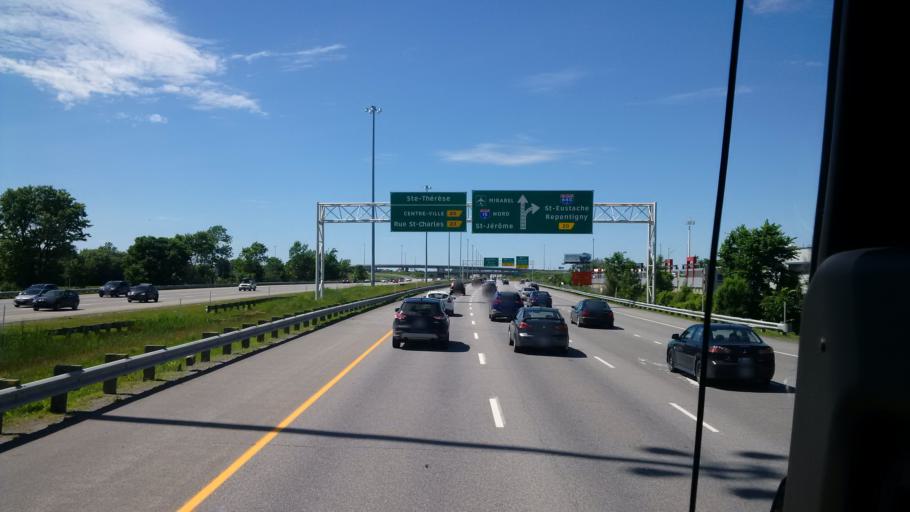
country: CA
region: Quebec
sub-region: Laurentides
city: Boisbriand
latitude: 45.6219
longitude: -73.8321
